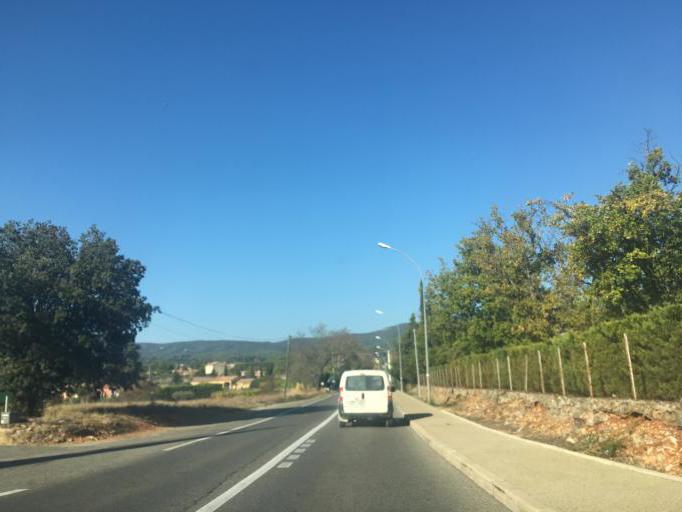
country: FR
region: Provence-Alpes-Cote d'Azur
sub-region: Departement du Var
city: Aups
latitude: 43.6179
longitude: 6.2204
